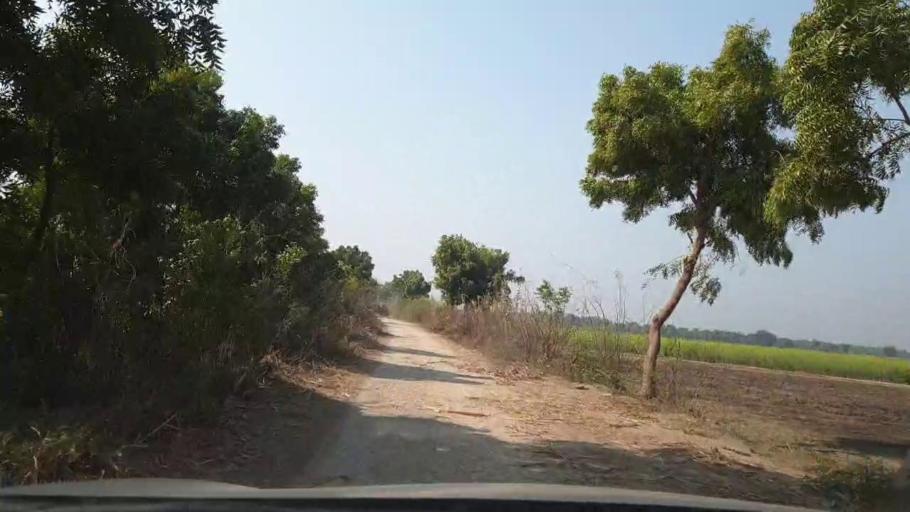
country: PK
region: Sindh
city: Tando Allahyar
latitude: 25.5301
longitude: 68.7636
